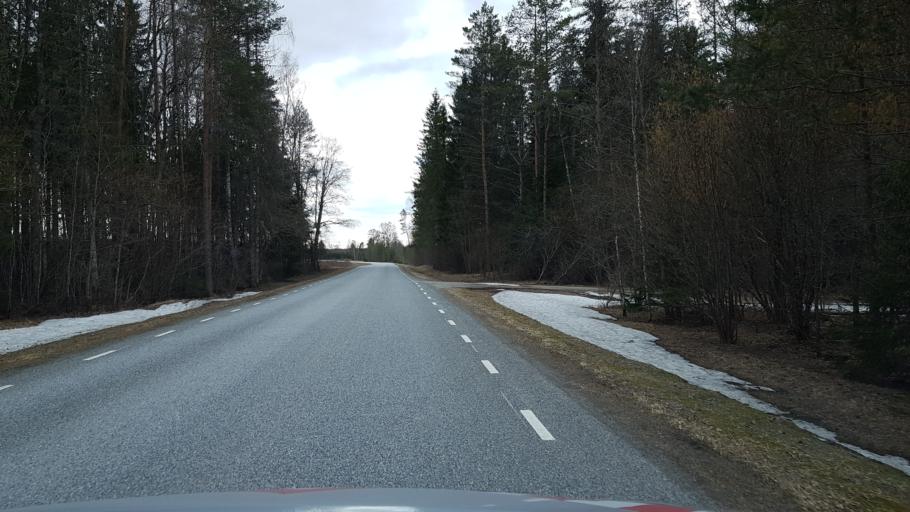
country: EE
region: Laeaene-Virumaa
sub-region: Tamsalu vald
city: Tamsalu
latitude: 59.2300
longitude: 26.1678
